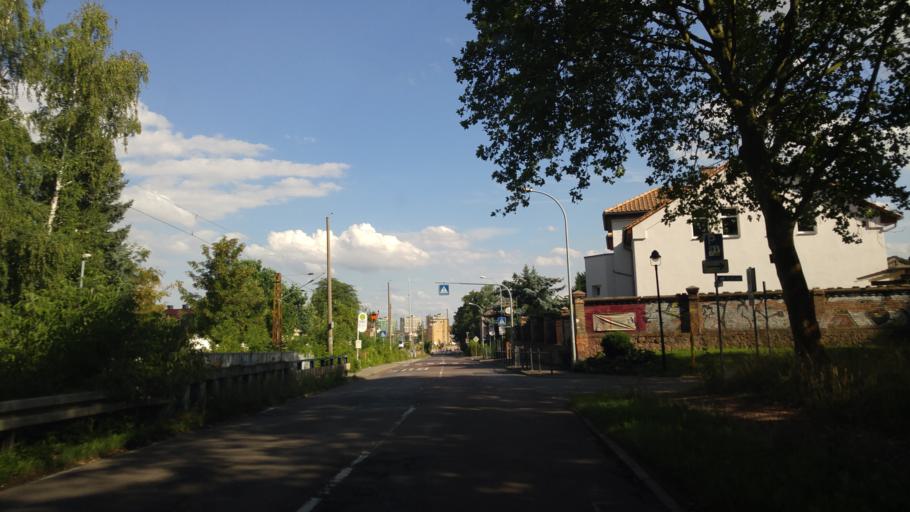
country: DE
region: Saxony-Anhalt
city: Halle Neustadt
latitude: 51.4900
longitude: 11.9033
